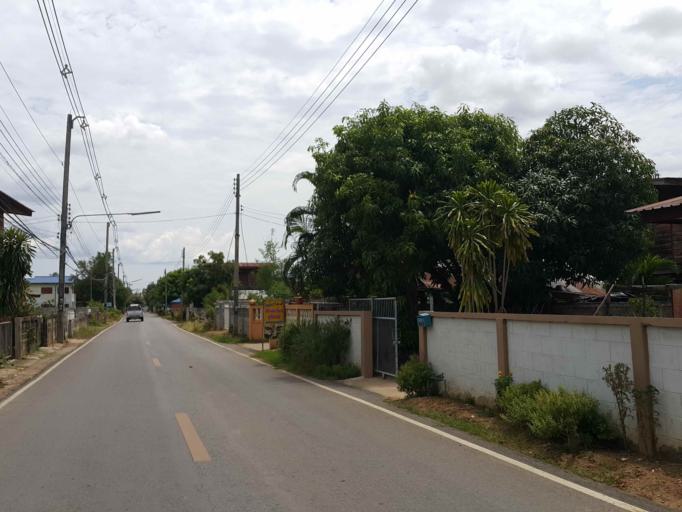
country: TH
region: Sukhothai
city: Thung Saliam
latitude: 17.3197
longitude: 99.5483
